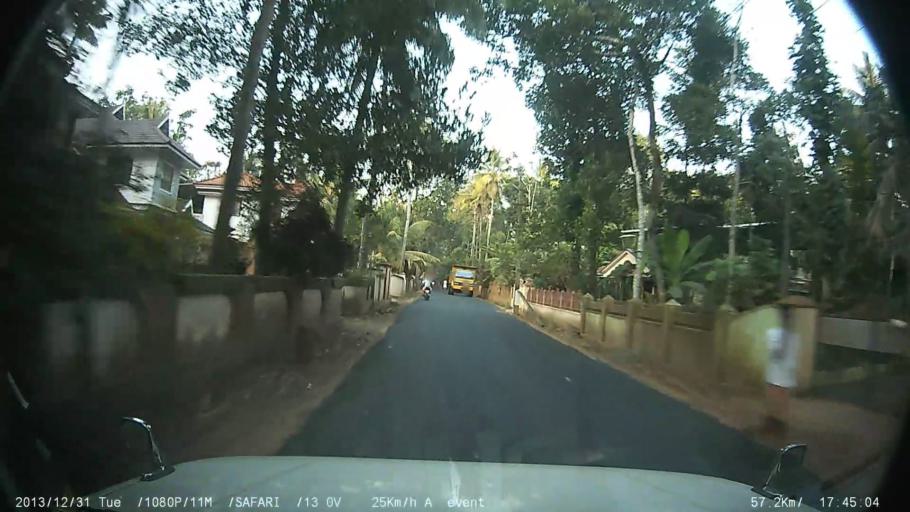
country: IN
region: Kerala
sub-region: Kottayam
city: Vaikam
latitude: 9.7288
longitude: 76.4778
